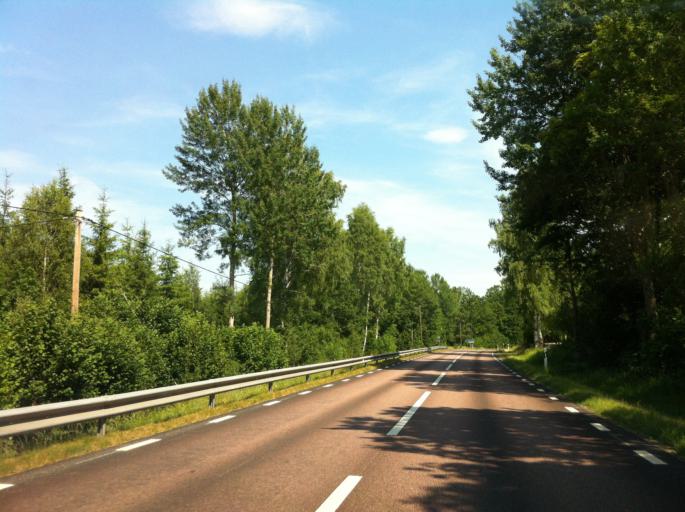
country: SE
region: Kalmar
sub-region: Nybro Kommun
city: Nybro
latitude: 56.7826
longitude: 15.8178
